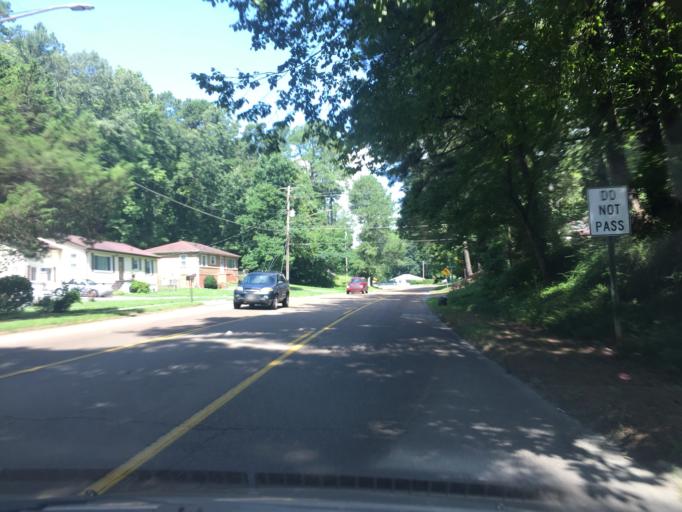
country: US
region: Tennessee
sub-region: Hamilton County
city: East Chattanooga
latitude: 35.0458
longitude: -85.2330
